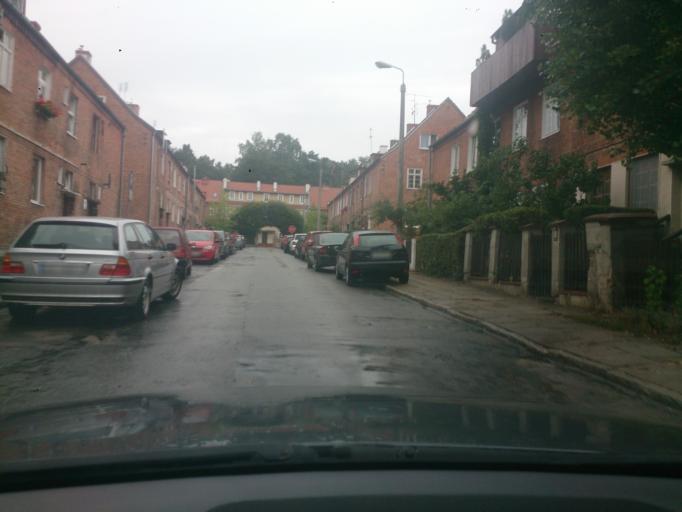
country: PL
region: Pomeranian Voivodeship
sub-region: Sopot
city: Sopot
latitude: 54.4498
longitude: 18.5527
